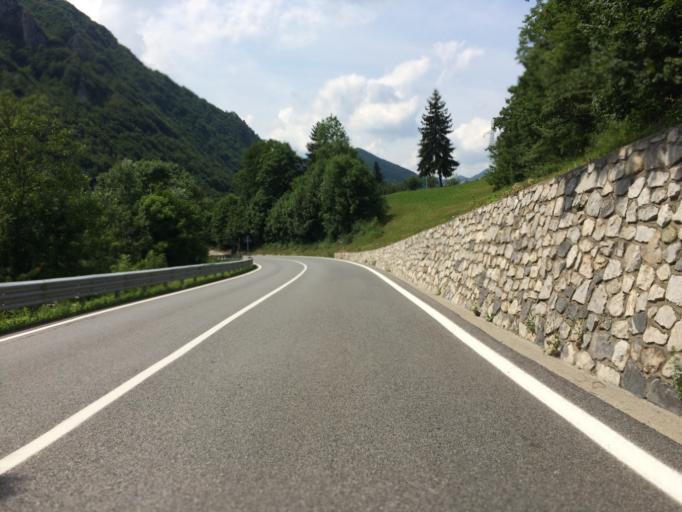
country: IT
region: Piedmont
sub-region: Provincia di Cuneo
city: Vernante
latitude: 44.2332
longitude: 7.5504
